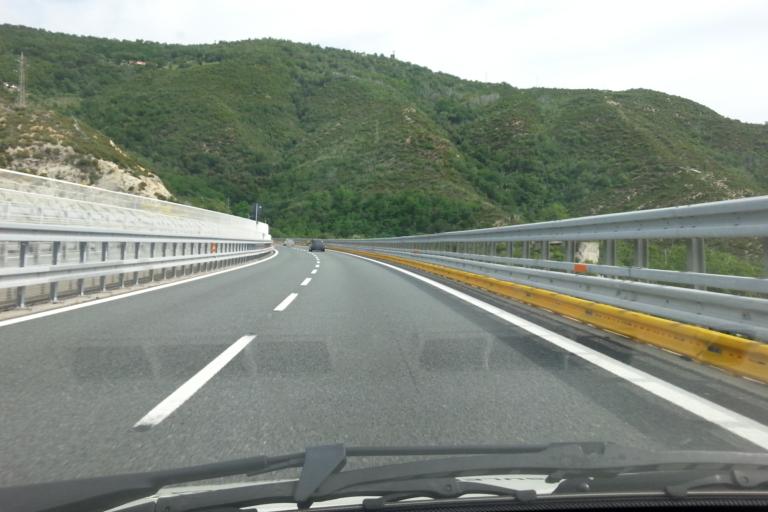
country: IT
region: Liguria
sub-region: Provincia di Savona
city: Spotorno
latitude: 44.2328
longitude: 8.3997
